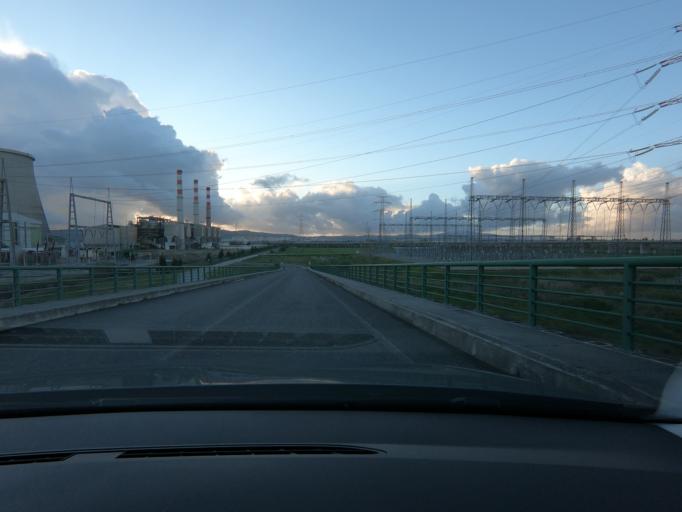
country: PT
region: Lisbon
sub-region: Alenquer
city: Carregado
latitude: 39.0122
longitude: -8.9499
